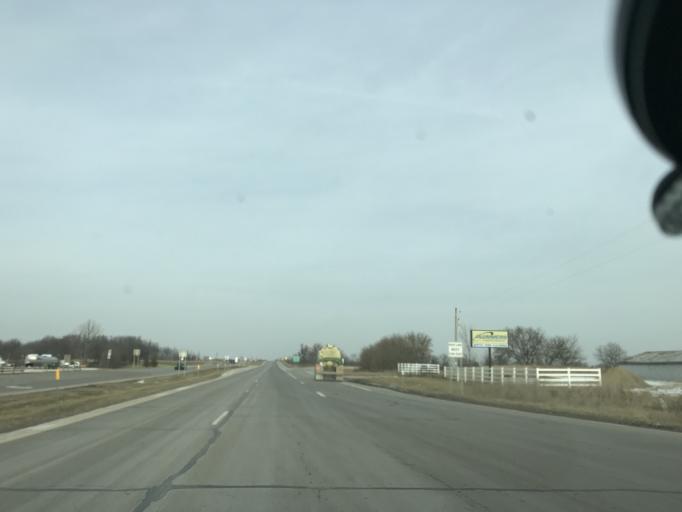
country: US
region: Michigan
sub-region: Ionia County
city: Lake Odessa
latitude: 42.8745
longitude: -85.0749
